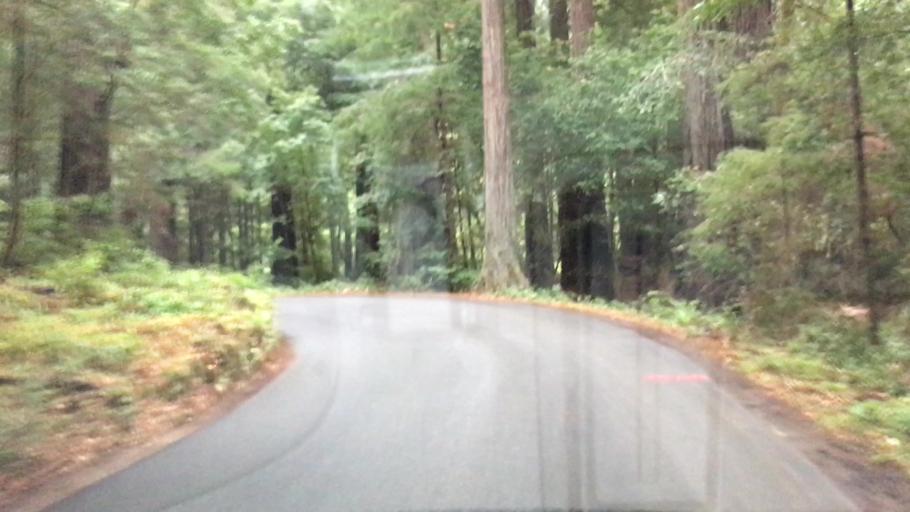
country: US
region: California
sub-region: Humboldt County
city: Rio Dell
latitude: 40.3521
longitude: -123.9829
